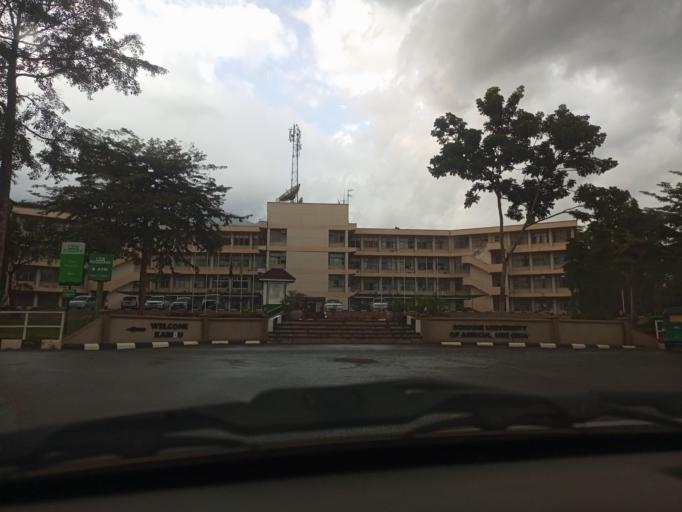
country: TZ
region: Morogoro
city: Morogoro
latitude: -6.8515
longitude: 37.6576
